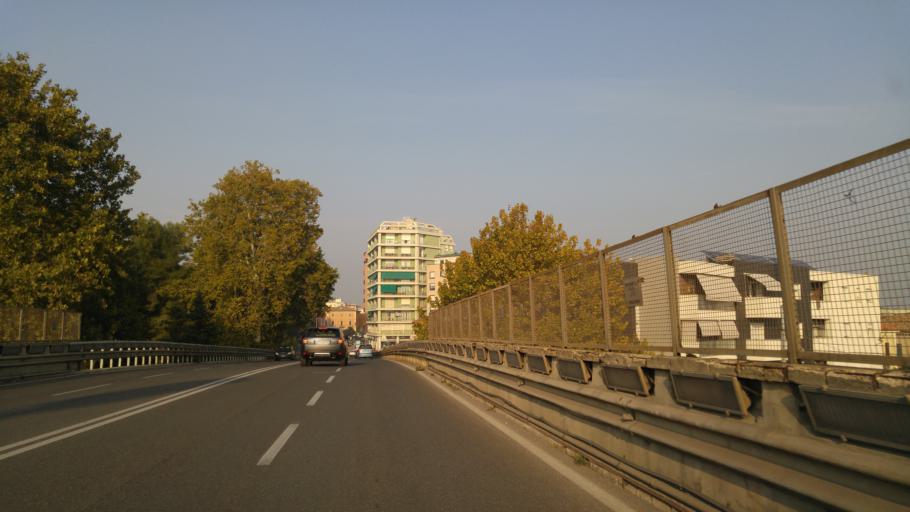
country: IT
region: The Marches
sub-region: Provincia di Pesaro e Urbino
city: Pesaro
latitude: 43.9055
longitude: 12.9069
